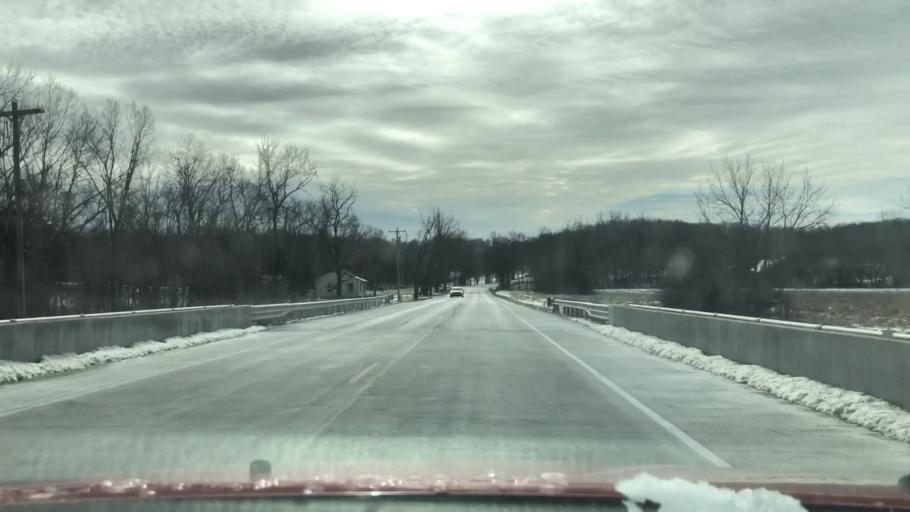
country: US
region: Missouri
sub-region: Jackson County
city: Oak Grove
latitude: 38.9437
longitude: -94.1320
